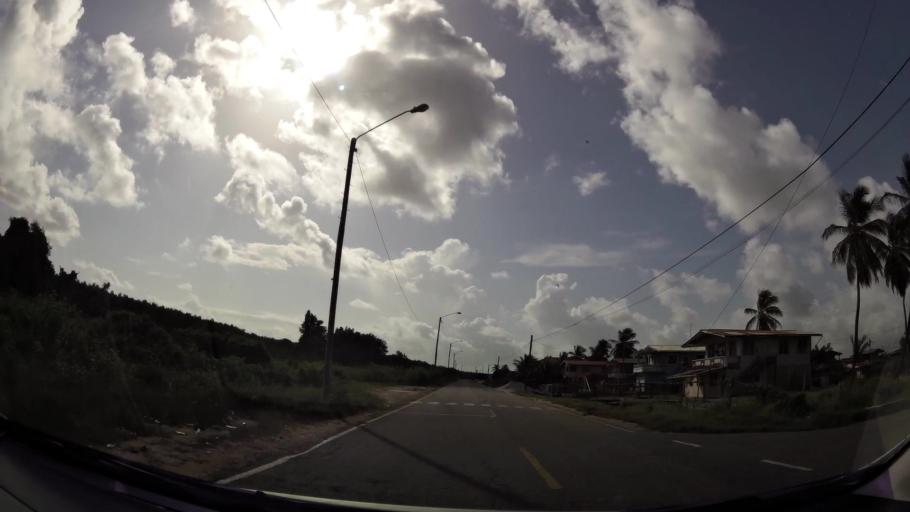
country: GY
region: Demerara-Mahaica
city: Mahaica Village
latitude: 6.7464
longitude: -57.9587
